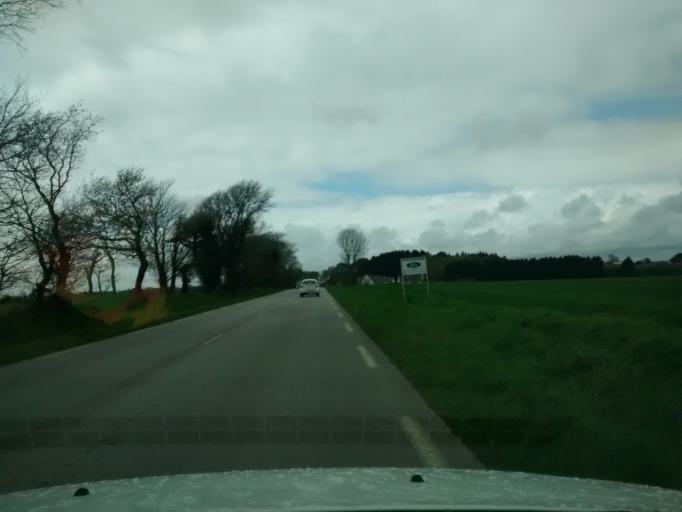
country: FR
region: Brittany
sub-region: Departement du Morbihan
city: Queven
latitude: 47.7727
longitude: -3.4124
